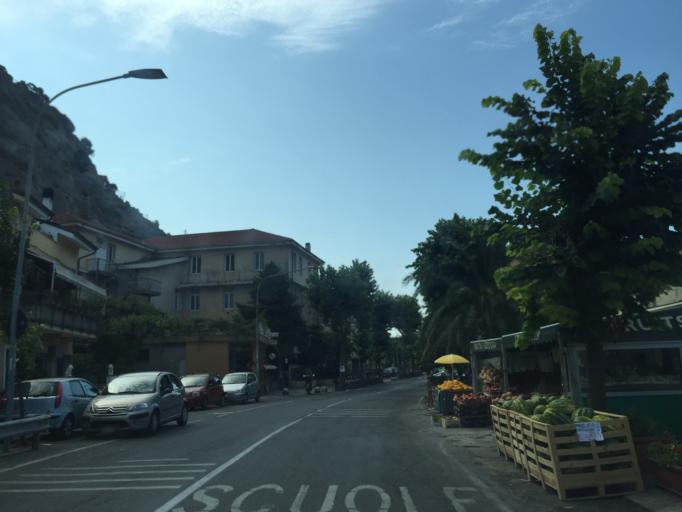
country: IT
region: Liguria
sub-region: Provincia di Imperia
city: Ventimiglia
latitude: 43.8036
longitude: 7.5977
